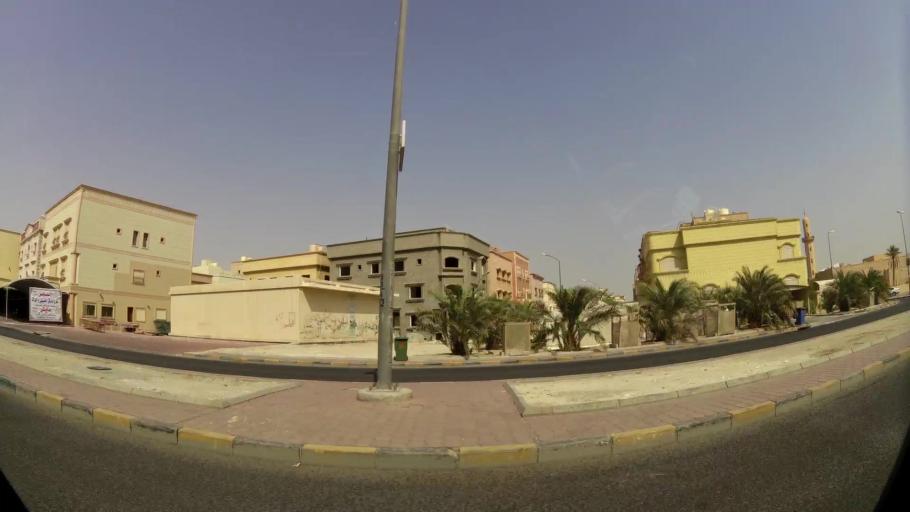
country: KW
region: Muhafazat al Jahra'
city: Al Jahra'
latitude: 29.3070
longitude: 47.6929
